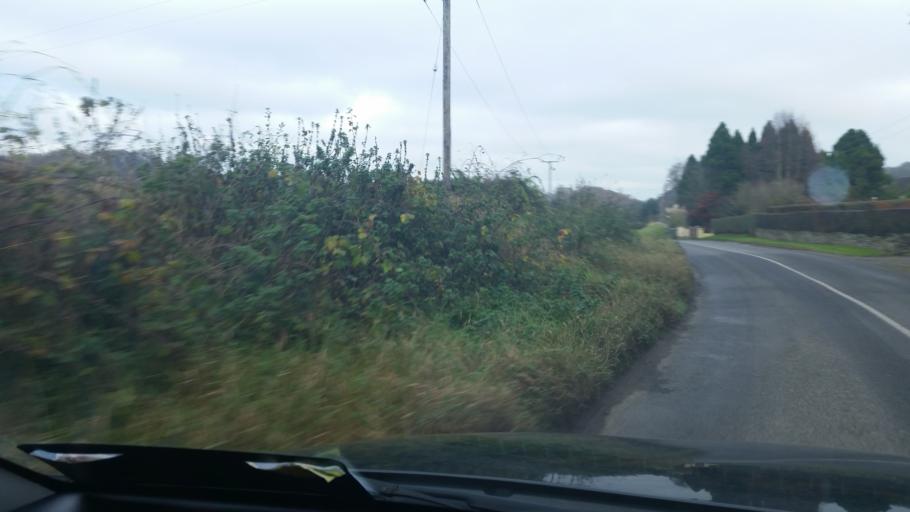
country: IE
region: Leinster
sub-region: Lu
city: Tullyallen
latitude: 53.6955
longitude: -6.4411
